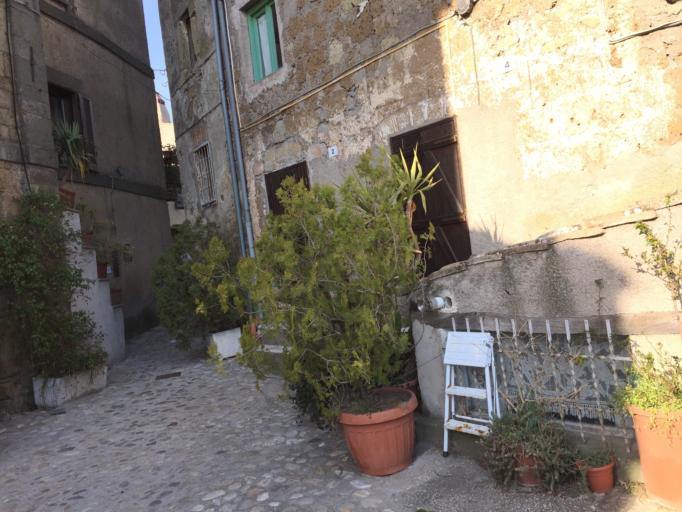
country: IT
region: Latium
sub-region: Provincia di Viterbo
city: Calcata Nuova
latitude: 42.2159
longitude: 12.4186
